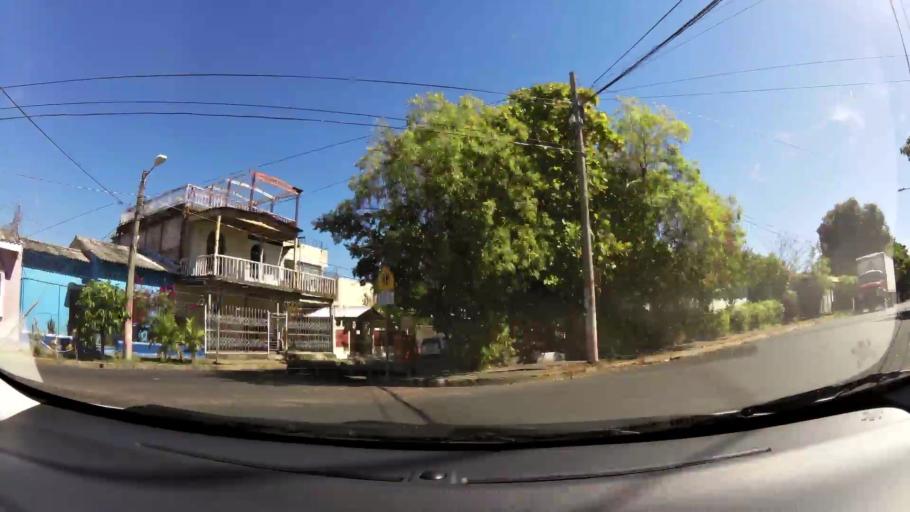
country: SV
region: San Miguel
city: San Miguel
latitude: 13.4780
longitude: -88.1700
